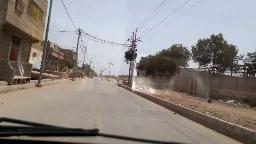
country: PK
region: Sindh
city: Malir Cantonment
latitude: 24.8386
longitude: 67.2046
